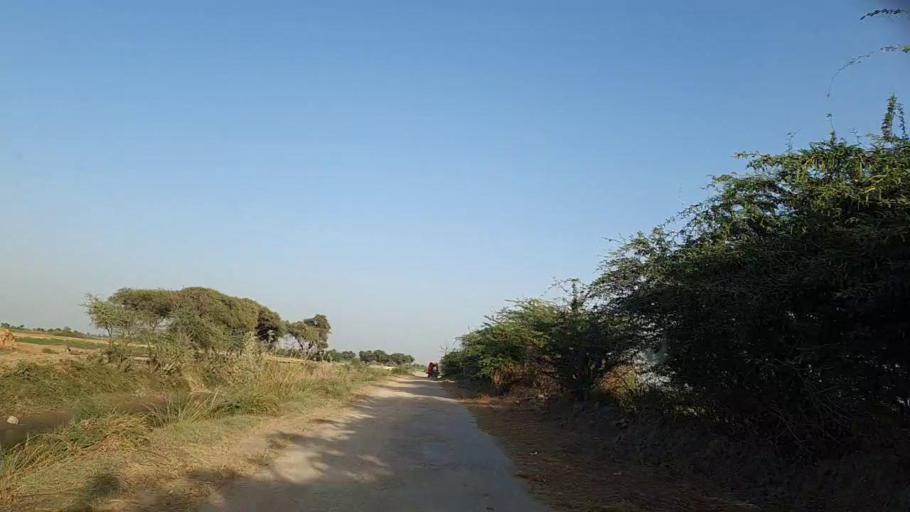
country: PK
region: Sindh
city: Jati
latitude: 24.4146
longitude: 68.3129
